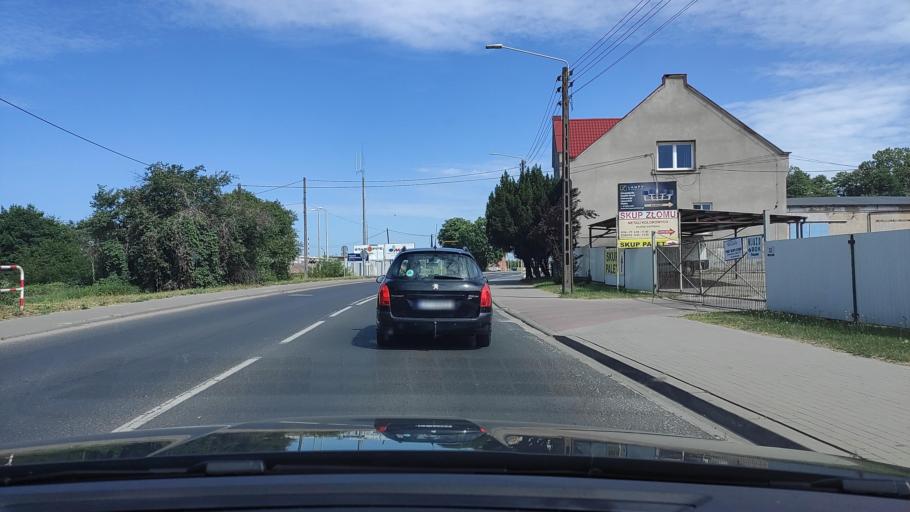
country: PL
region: Greater Poland Voivodeship
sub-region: Powiat poznanski
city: Czerwonak
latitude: 52.4659
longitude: 16.9808
